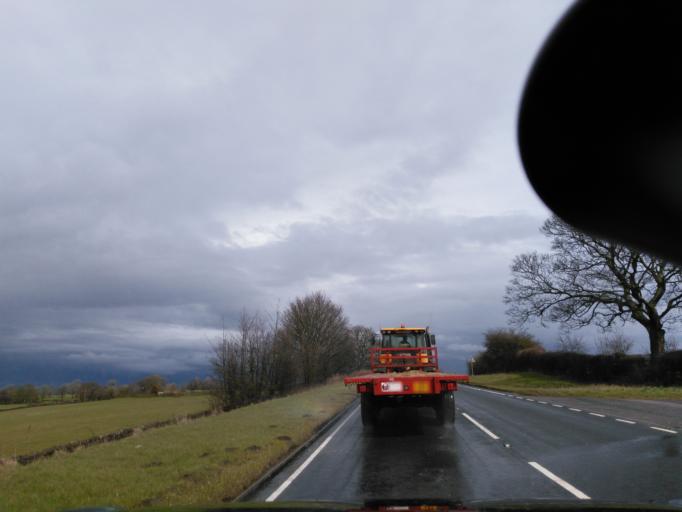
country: GB
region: England
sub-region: North Yorkshire
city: Stainburn
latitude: 54.0052
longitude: -1.6170
